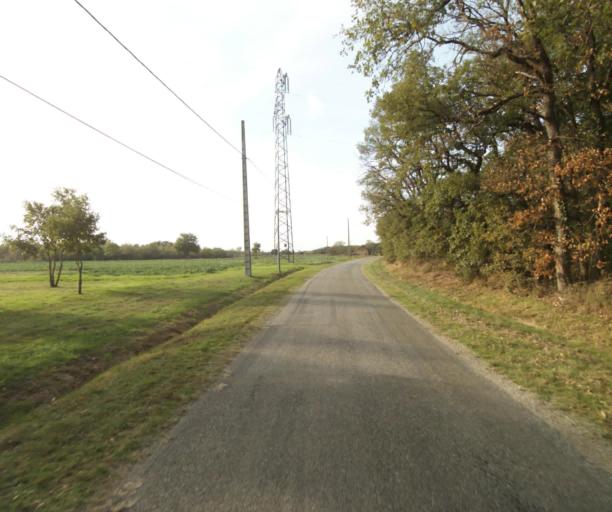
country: FR
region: Midi-Pyrenees
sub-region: Departement du Tarn-et-Garonne
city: Campsas
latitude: 43.8749
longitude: 1.3267
